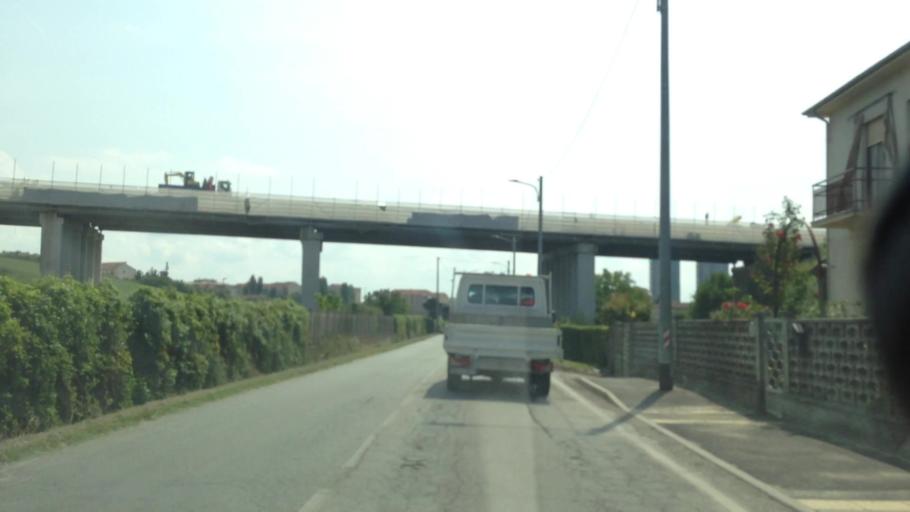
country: IT
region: Piedmont
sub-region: Provincia di Asti
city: Asti
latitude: 44.9125
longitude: 8.1807
